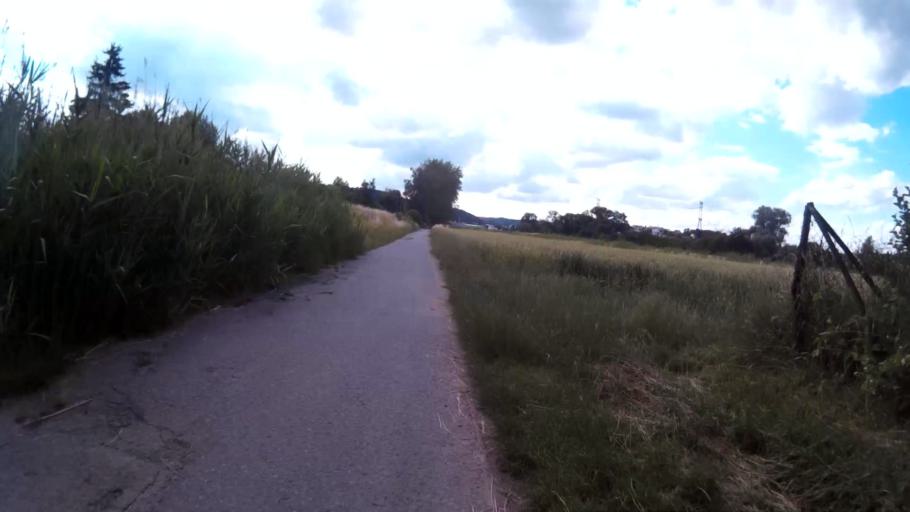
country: CZ
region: South Moravian
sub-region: Okres Brno-Venkov
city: Rosice
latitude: 49.1737
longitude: 16.4032
